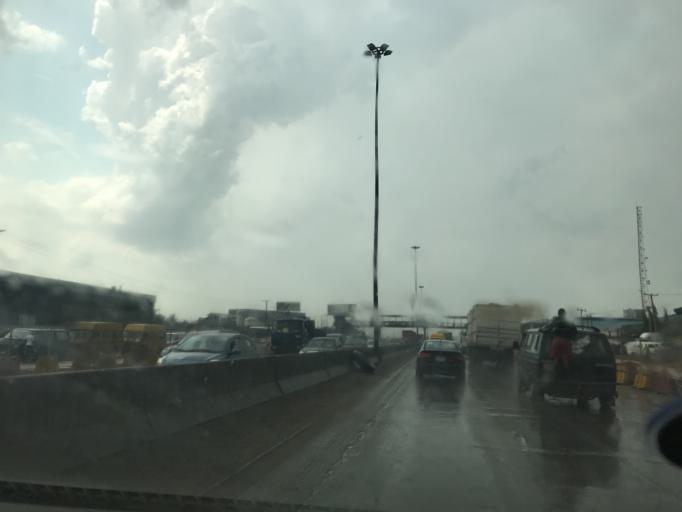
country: NG
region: Lagos
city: Oshodi
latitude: 6.5522
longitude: 3.3434
